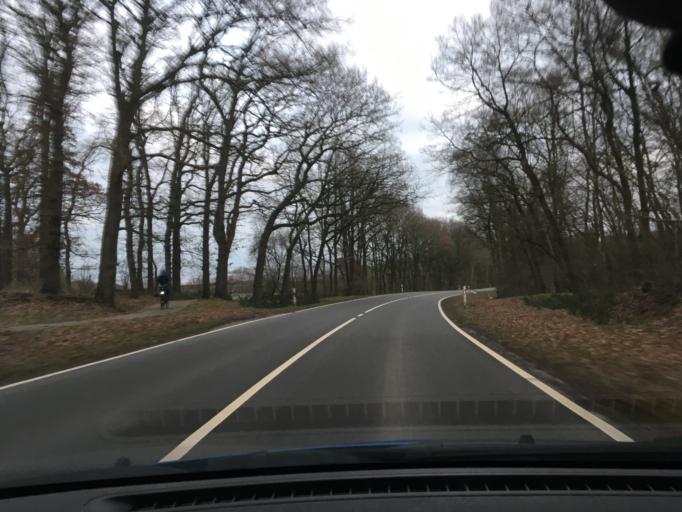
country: DE
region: Schleswig-Holstein
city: Kaaks
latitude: 53.9954
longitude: 9.4543
